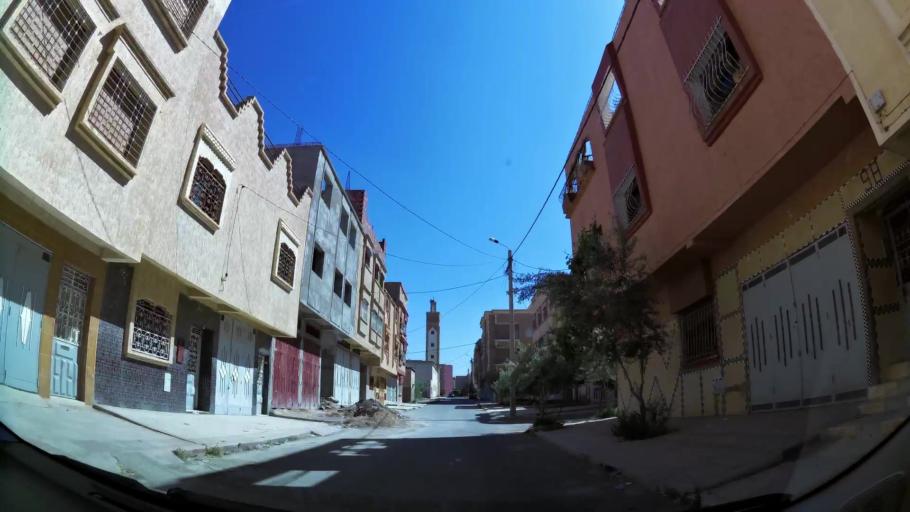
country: MA
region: Oriental
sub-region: Oujda-Angad
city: Oujda
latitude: 34.6840
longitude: -1.9438
